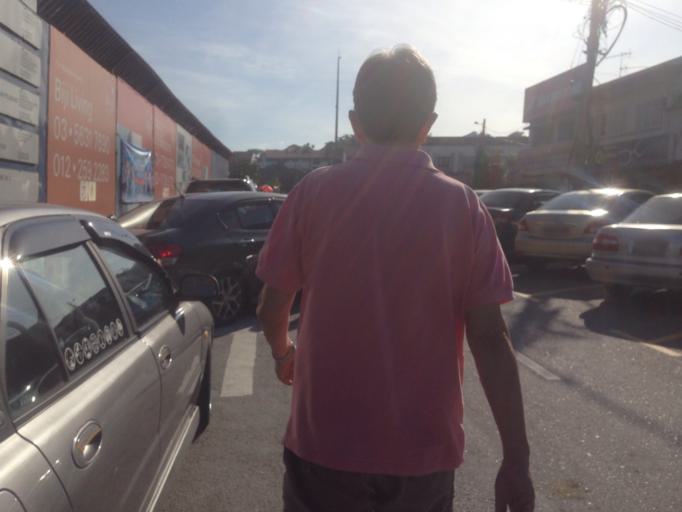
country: MY
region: Selangor
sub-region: Petaling
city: Petaling Jaya
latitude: 3.1284
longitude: 101.6346
